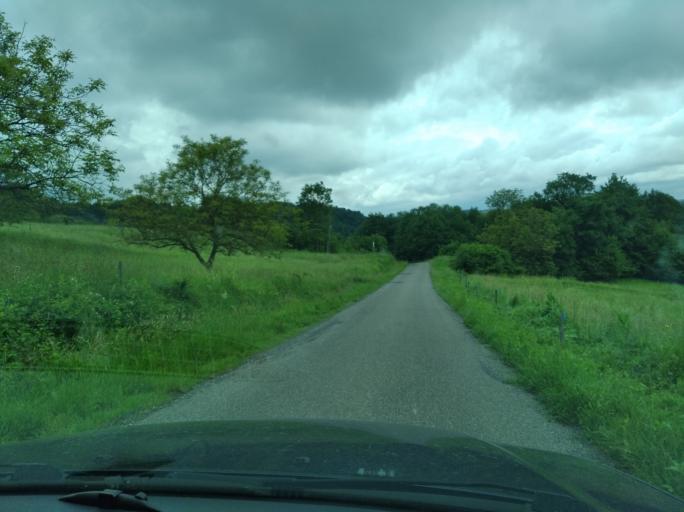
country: PL
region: Subcarpathian Voivodeship
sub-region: Powiat przemyski
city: Nienadowa
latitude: 49.8601
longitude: 22.4101
